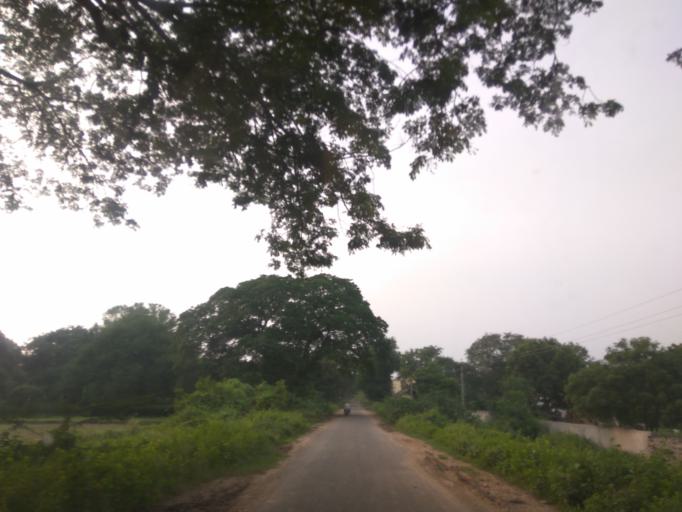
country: IN
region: Andhra Pradesh
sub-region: Guntur
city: Vinukonda
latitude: 16.1129
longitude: 79.7530
